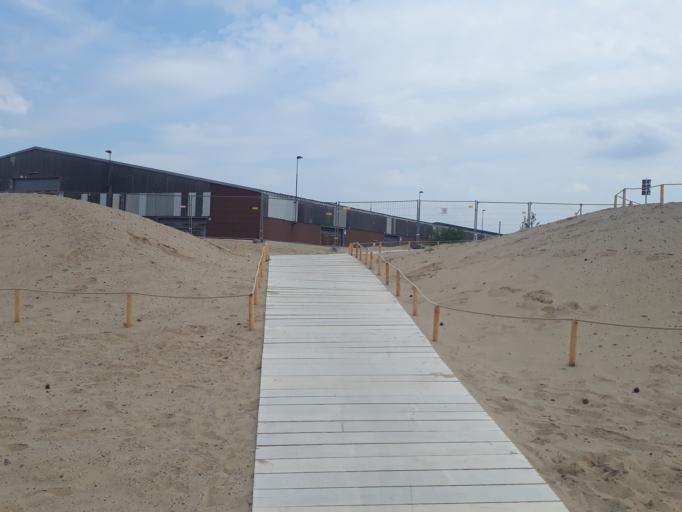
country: DE
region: Bremen
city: Bremen
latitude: 53.1048
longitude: 8.7546
